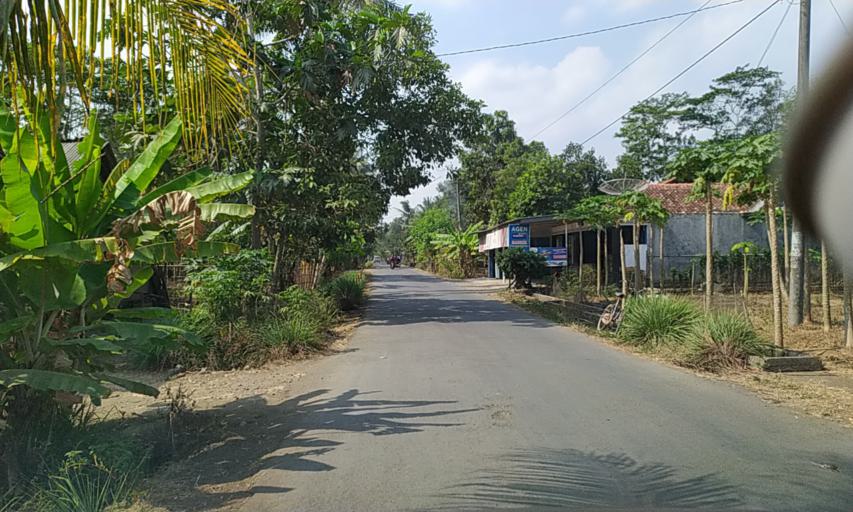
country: ID
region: Central Java
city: Kemantren Satu
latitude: -7.5270
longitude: 108.8824
